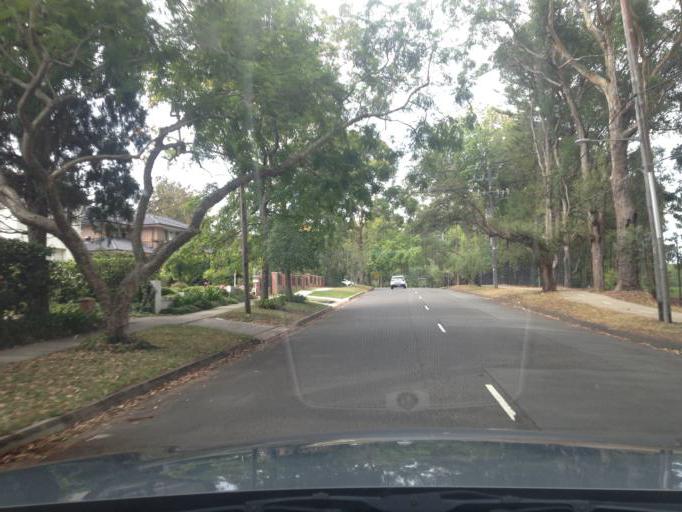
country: AU
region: New South Wales
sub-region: Ku-ring-gai
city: Killara
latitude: -33.7743
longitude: 151.1505
